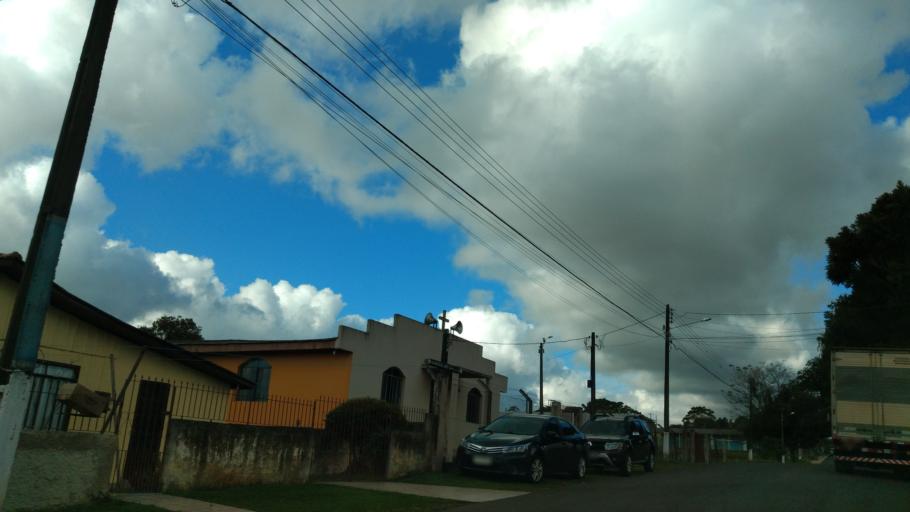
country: BR
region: Parana
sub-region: Guarapuava
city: Guarapuava
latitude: -25.3959
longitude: -51.4909
